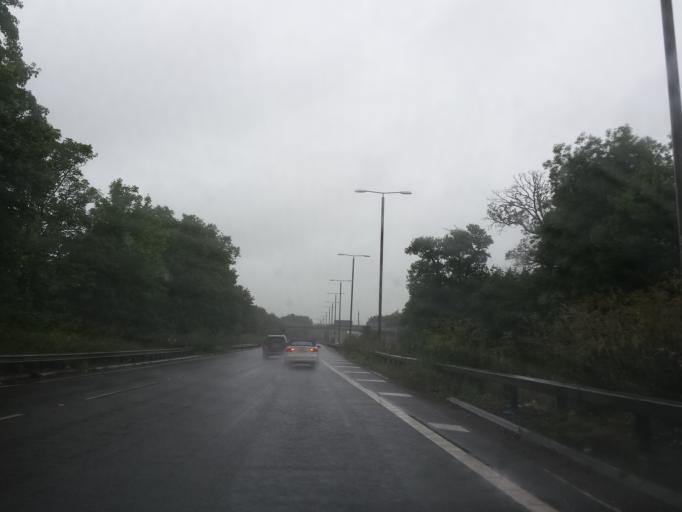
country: GB
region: England
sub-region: Leicestershire
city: Enderby
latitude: 52.6002
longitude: -1.1965
